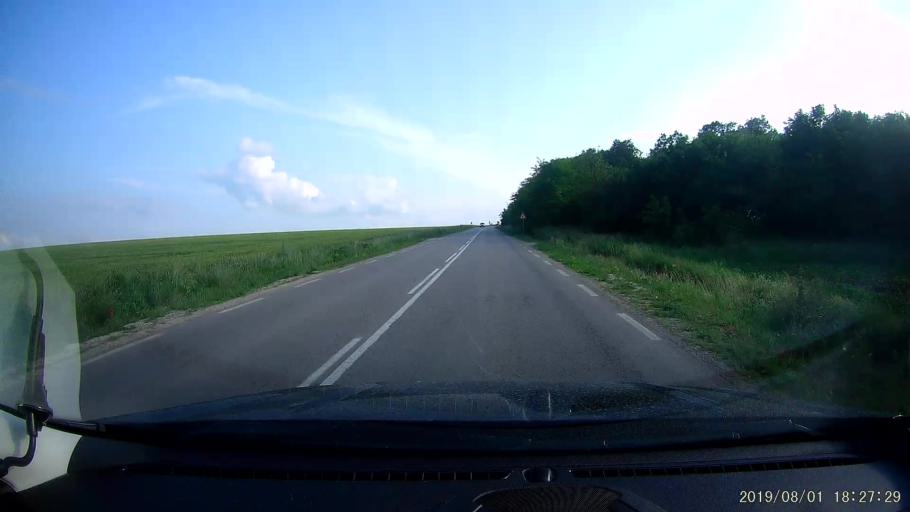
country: BG
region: Shumen
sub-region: Obshtina Venets
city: Venets
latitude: 43.5860
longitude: 26.9818
